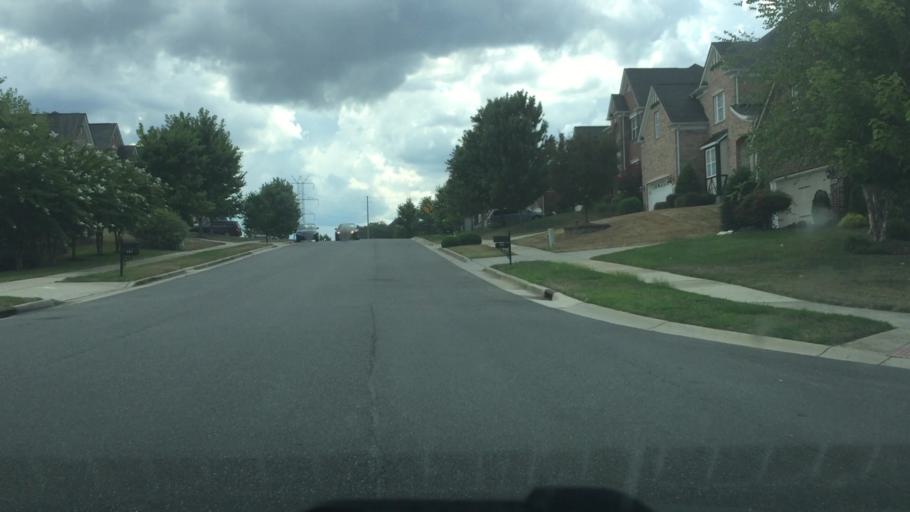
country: US
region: North Carolina
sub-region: Mecklenburg County
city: Huntersville
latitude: 35.4061
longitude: -80.7515
